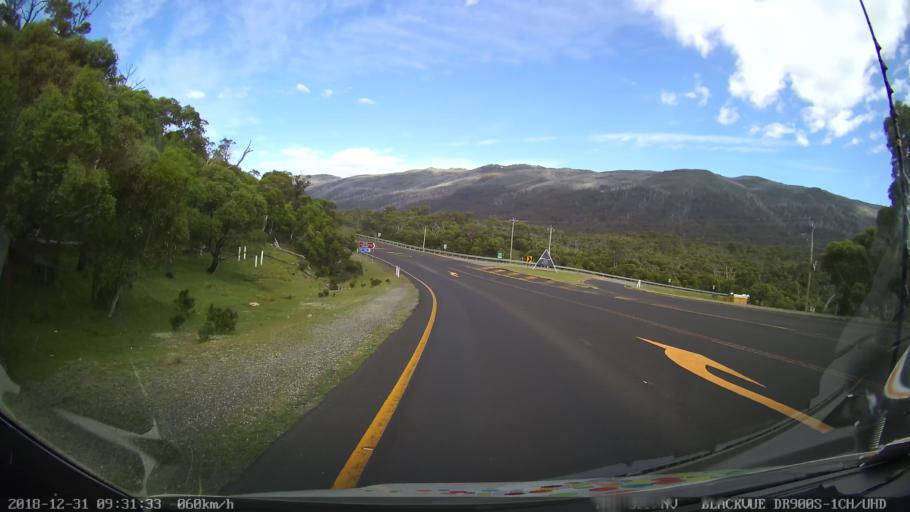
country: AU
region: New South Wales
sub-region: Snowy River
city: Jindabyne
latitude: -36.4491
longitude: 148.4429
